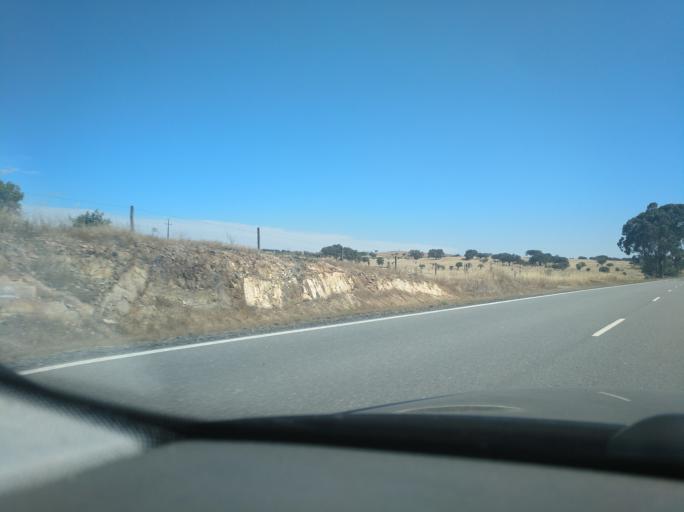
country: PT
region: Beja
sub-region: Castro Verde
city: Castro Verde
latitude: 37.6334
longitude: -8.0819
